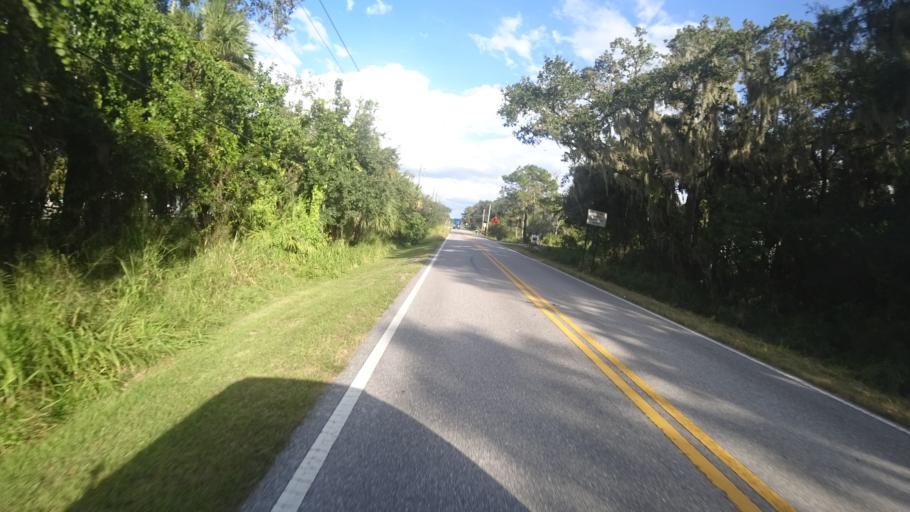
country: US
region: Florida
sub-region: Manatee County
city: Samoset
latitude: 27.4767
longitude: -82.5203
